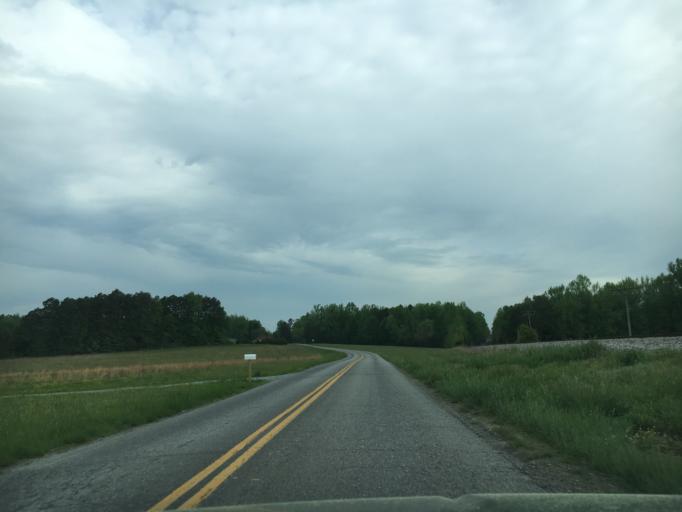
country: US
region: Virginia
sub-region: Campbell County
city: Brookneal
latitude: 36.9129
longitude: -78.9400
